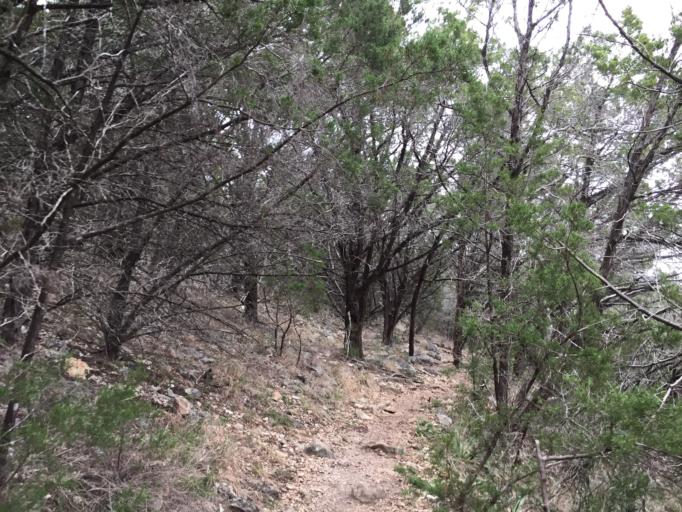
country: US
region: Texas
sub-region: Travis County
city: Rollingwood
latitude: 30.2489
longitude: -97.8207
